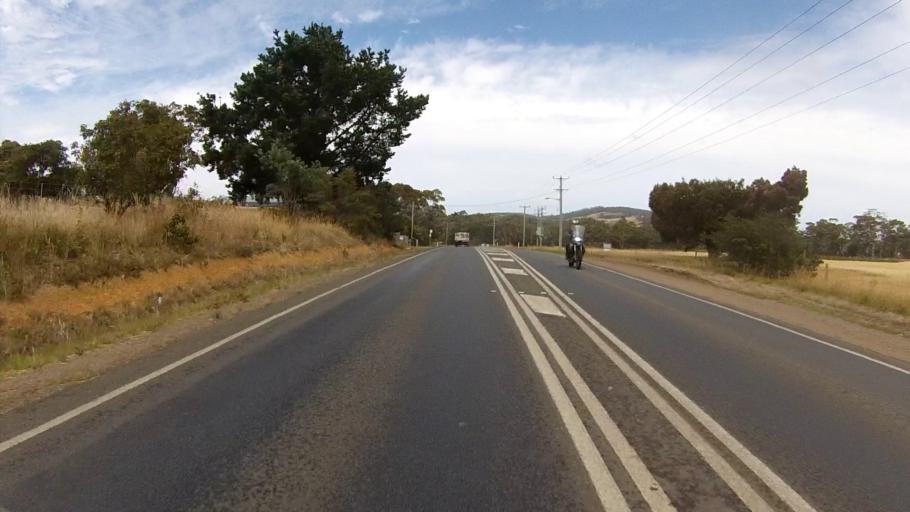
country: AU
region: Tasmania
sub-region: Clarence
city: Sandford
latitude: -42.9336
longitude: 147.4918
